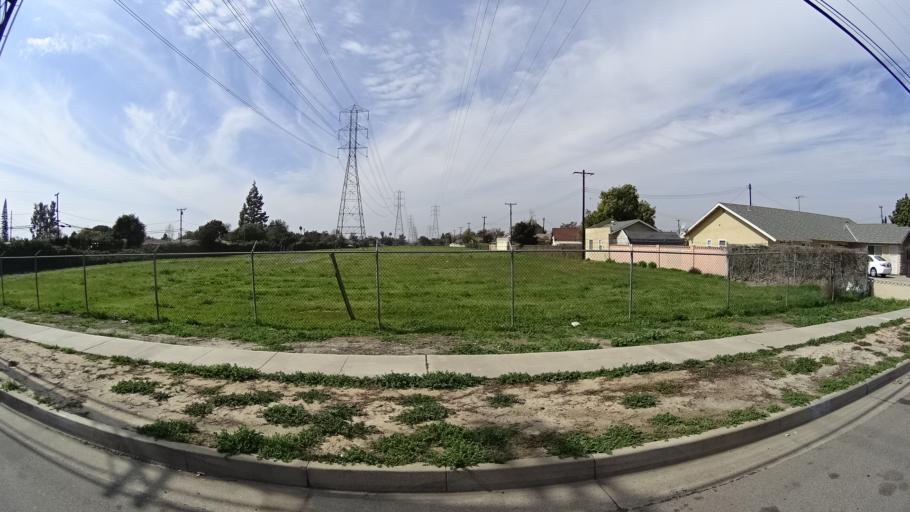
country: US
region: California
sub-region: Orange County
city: Garden Grove
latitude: 33.8072
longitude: -117.9502
